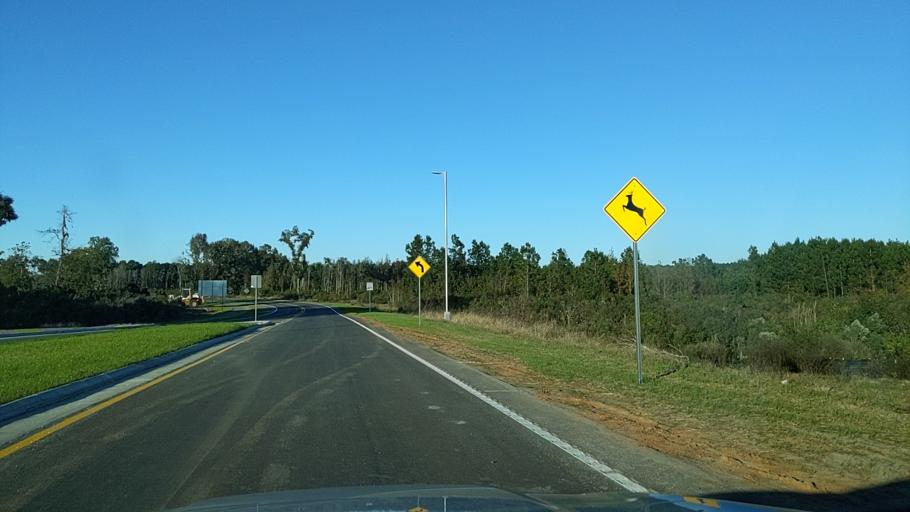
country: US
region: Georgia
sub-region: Chatham County
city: Port Wentworth
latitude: 32.1867
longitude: -81.2207
